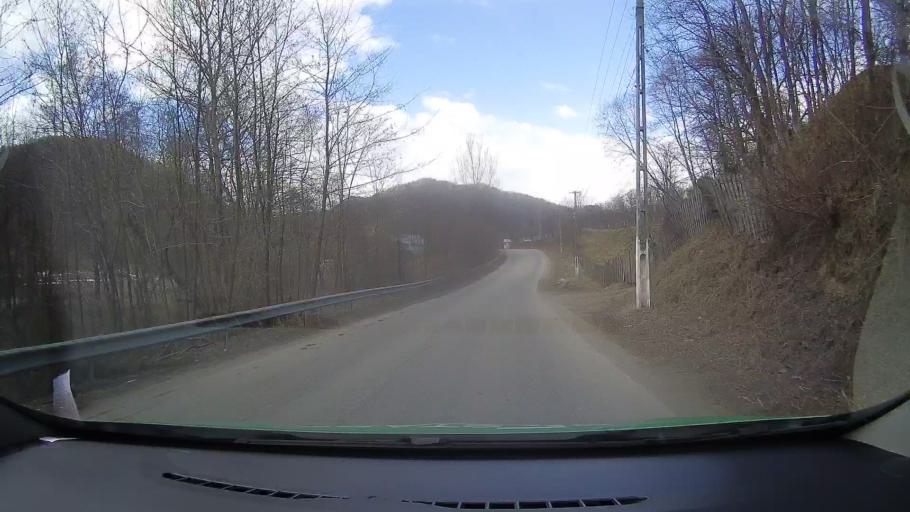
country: RO
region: Dambovita
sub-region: Comuna Varfuri
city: Varfuri
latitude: 45.0792
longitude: 25.5142
